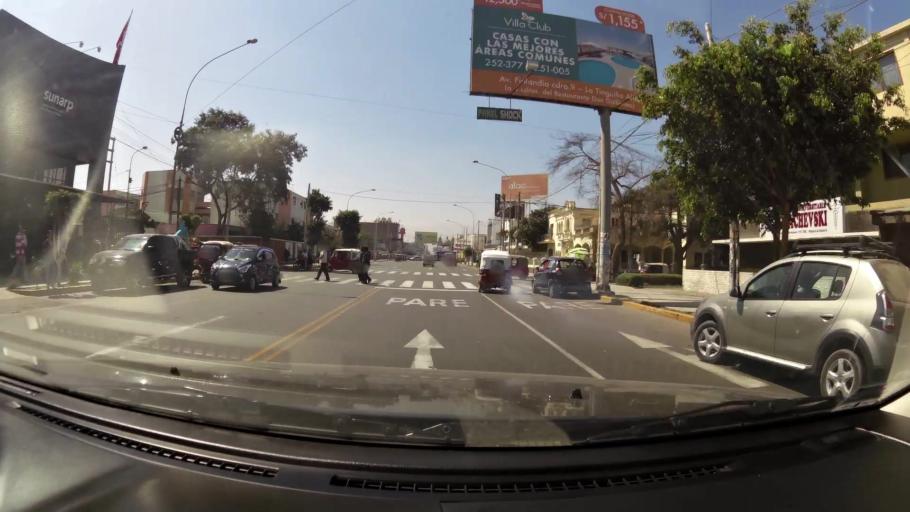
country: PE
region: Ica
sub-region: Provincia de Ica
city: Ica
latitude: -14.0656
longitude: -75.7368
